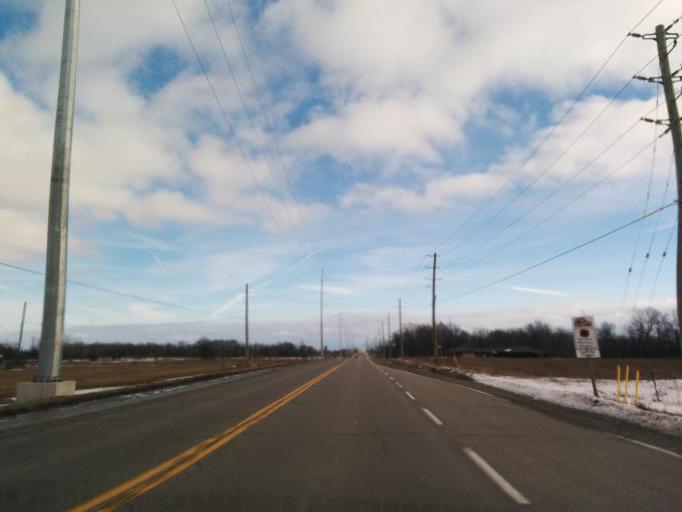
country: CA
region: Ontario
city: Ancaster
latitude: 42.9491
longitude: -80.0158
